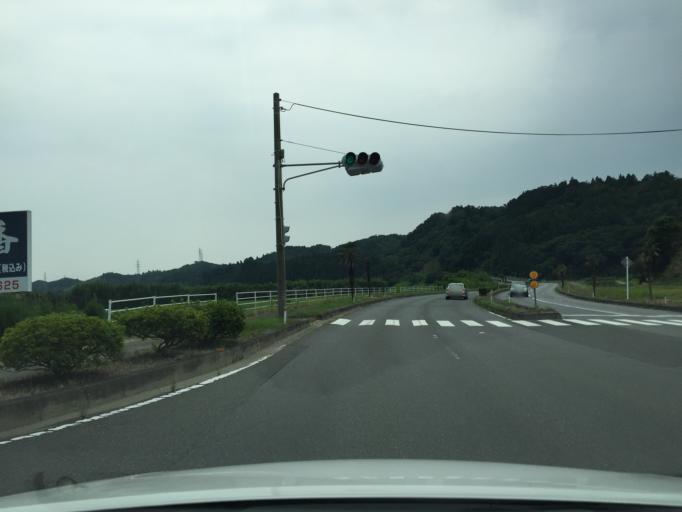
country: JP
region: Fukushima
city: Iwaki
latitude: 36.9927
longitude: 140.8254
